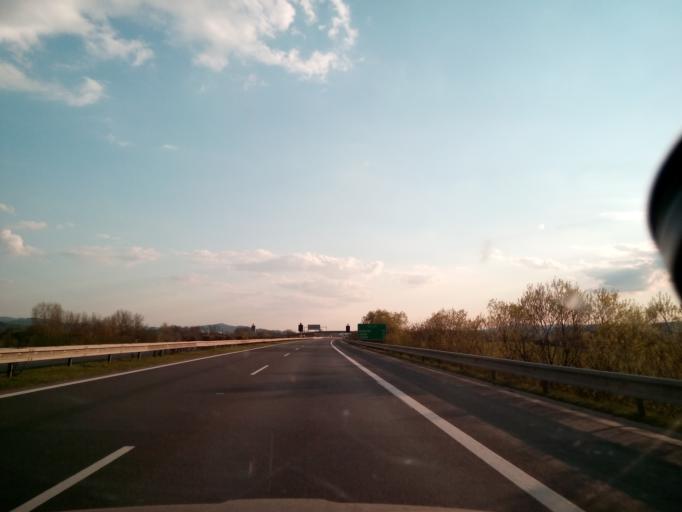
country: SK
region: Nitriansky
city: Ilava
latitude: 48.9954
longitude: 18.2127
